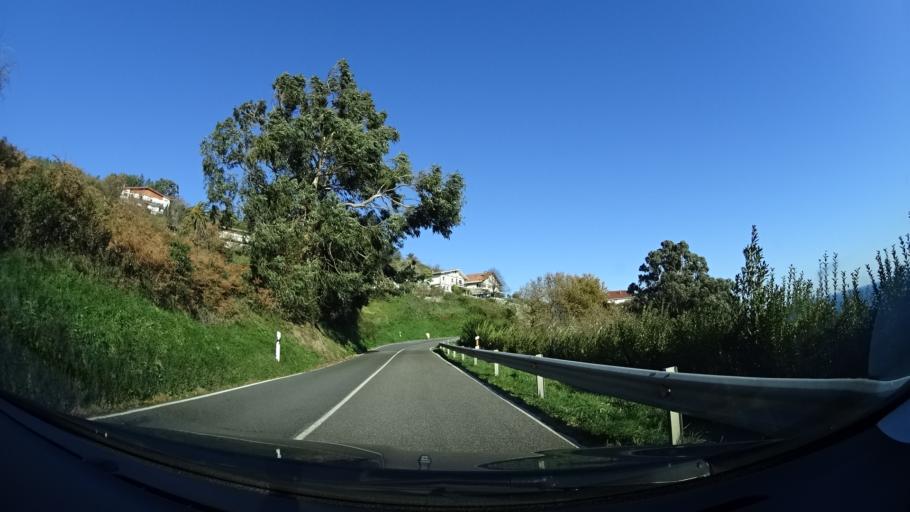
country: ES
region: Basque Country
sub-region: Bizkaia
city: Bermeo
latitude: 43.4246
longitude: -2.7411
